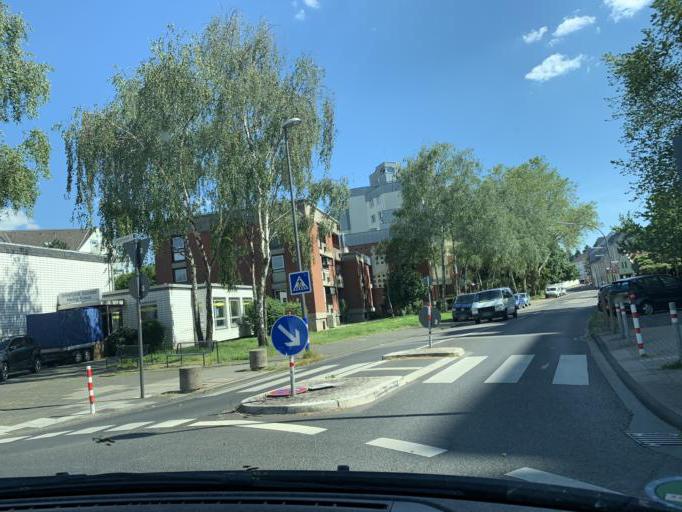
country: DE
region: North Rhine-Westphalia
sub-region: Regierungsbezirk Koln
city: Bilderstoeckchen
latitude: 50.9831
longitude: 6.9441
